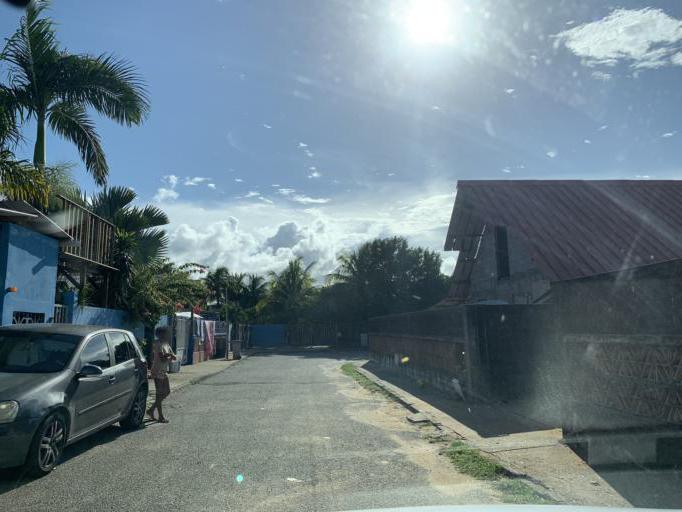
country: GF
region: Guyane
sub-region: Guyane
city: Kourou
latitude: 5.1748
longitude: -52.6462
